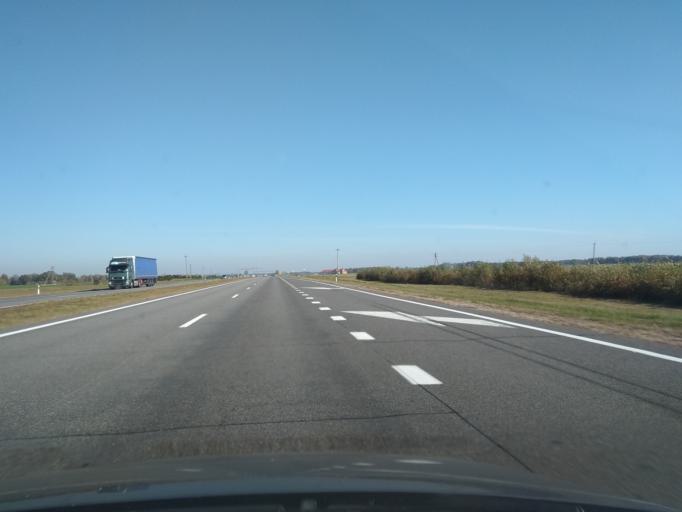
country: BY
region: Brest
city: Byaroza
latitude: 52.4907
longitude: 24.9710
